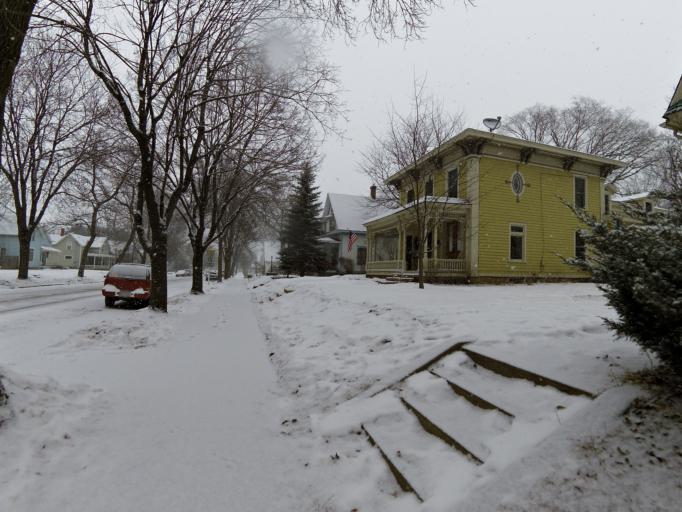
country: US
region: Wisconsin
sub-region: Saint Croix County
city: Hudson
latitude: 44.9804
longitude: -92.7539
